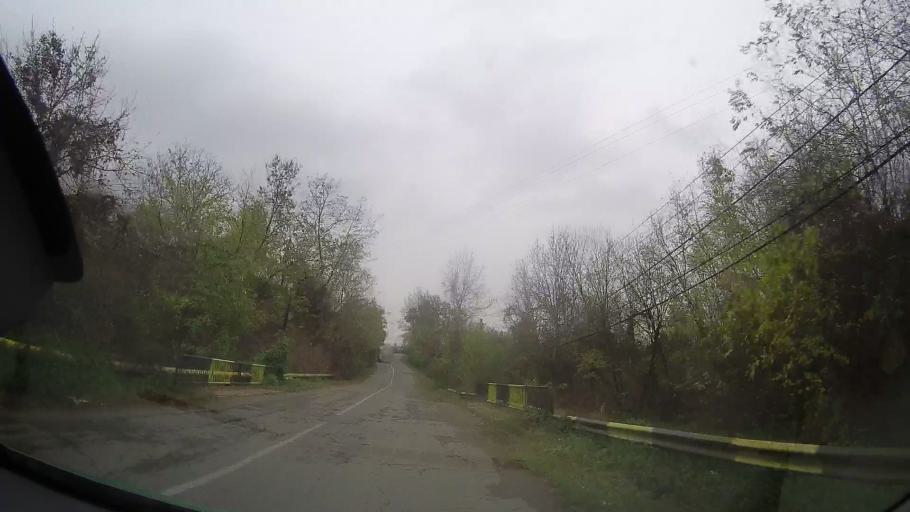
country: RO
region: Prahova
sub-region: Comuna Ceptura
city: Ceptura de Jos
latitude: 45.0323
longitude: 26.3197
